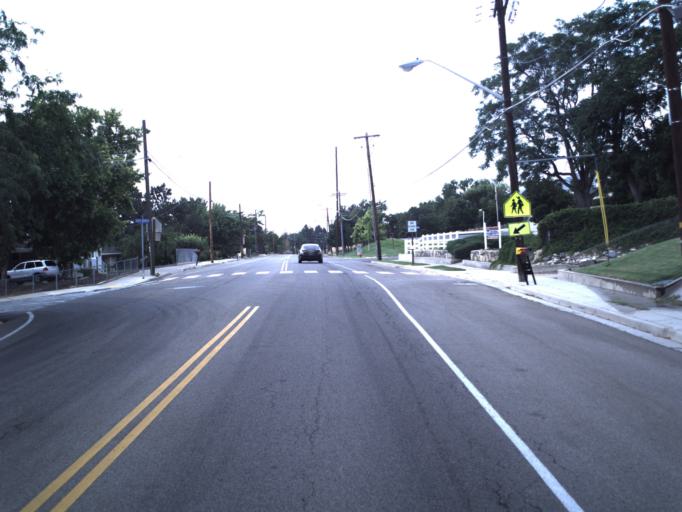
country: US
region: Utah
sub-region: Davis County
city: Centerville
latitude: 40.9470
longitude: -111.8817
